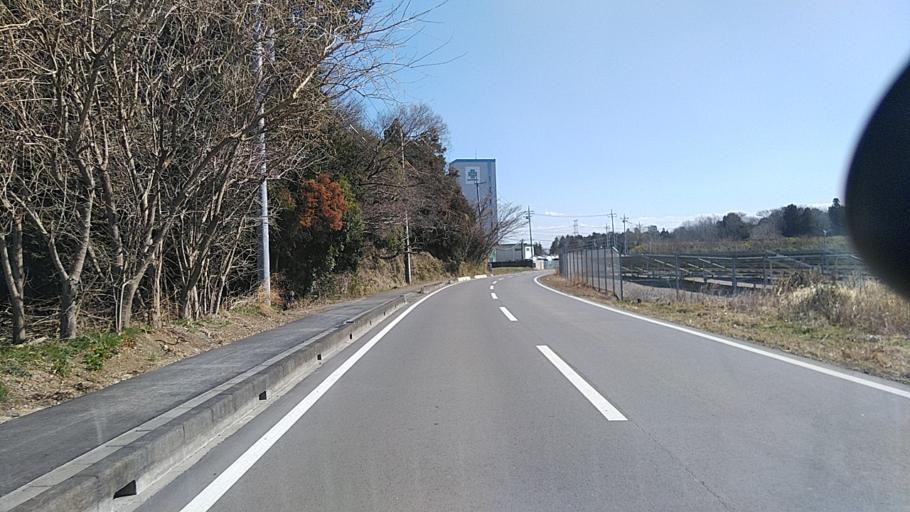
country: JP
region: Ibaraki
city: Ishige
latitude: 36.0880
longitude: 140.0221
